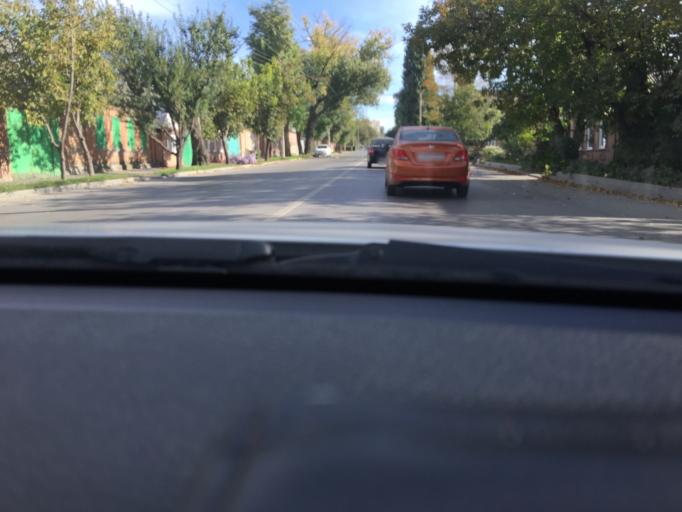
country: RU
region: Rostov
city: Imeni Chkalova
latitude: 47.2651
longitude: 39.7804
